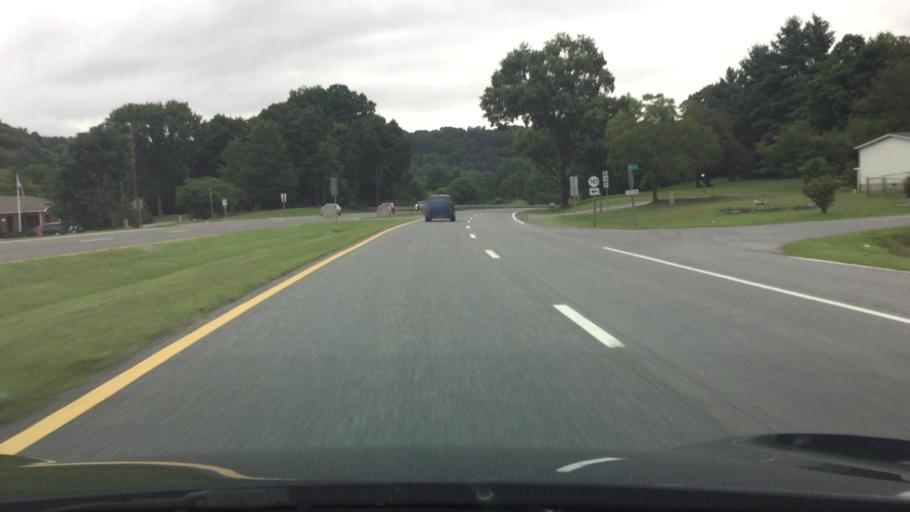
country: US
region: Virginia
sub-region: Montgomery County
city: Shawsville
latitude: 37.2197
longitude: -80.2289
